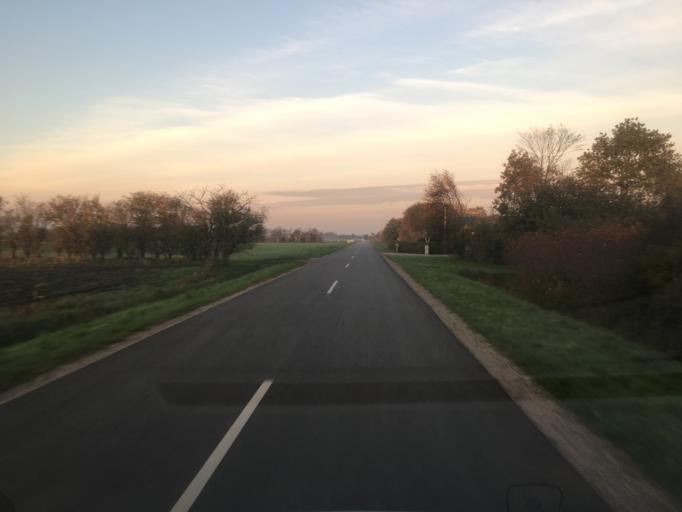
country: DK
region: South Denmark
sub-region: Tonder Kommune
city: Logumkloster
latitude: 55.0621
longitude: 9.0140
